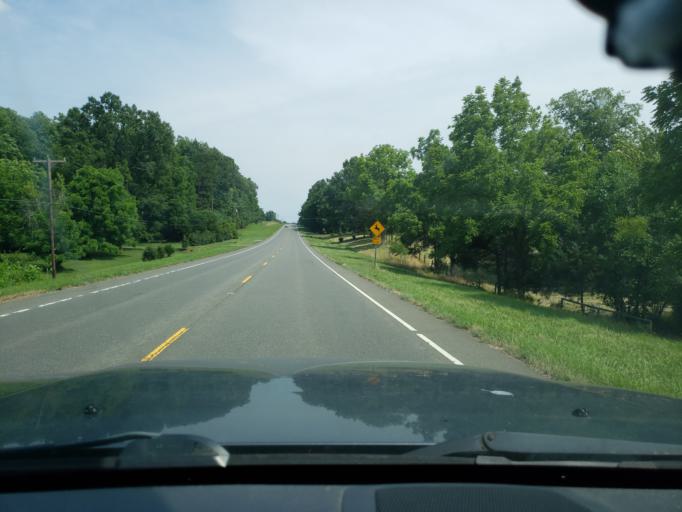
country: US
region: North Carolina
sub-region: Alamance County
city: Saxapahaw
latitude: 35.9582
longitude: -79.2625
